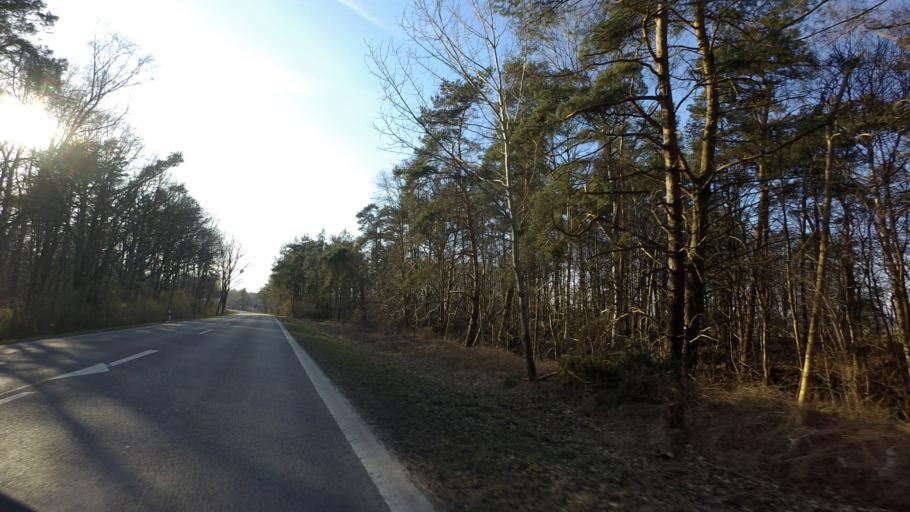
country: DE
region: Brandenburg
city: Althuttendorf
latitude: 52.9515
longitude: 13.8166
